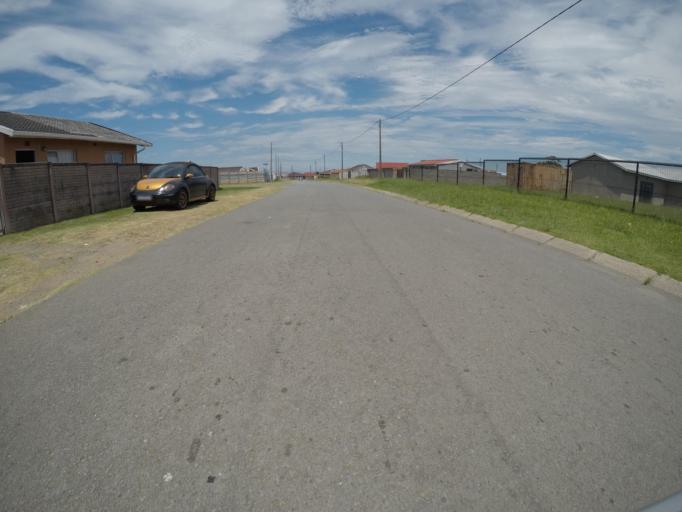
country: ZA
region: Eastern Cape
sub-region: Buffalo City Metropolitan Municipality
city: East London
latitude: -33.0461
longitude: 27.8492
